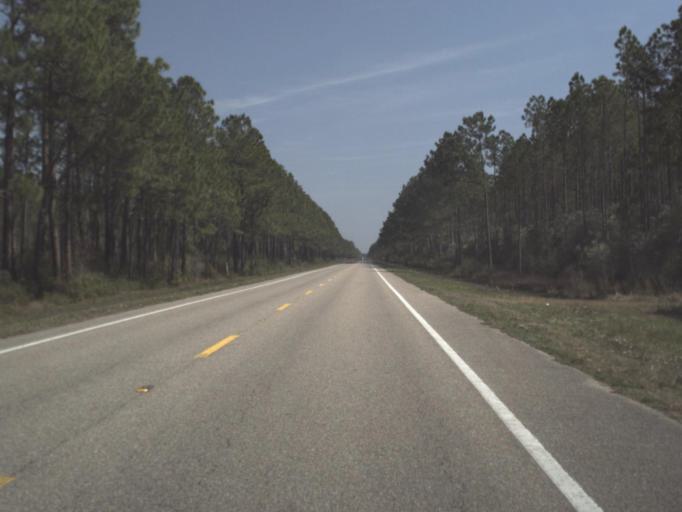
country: US
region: Florida
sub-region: Franklin County
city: Apalachicola
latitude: 29.7336
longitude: -85.1491
